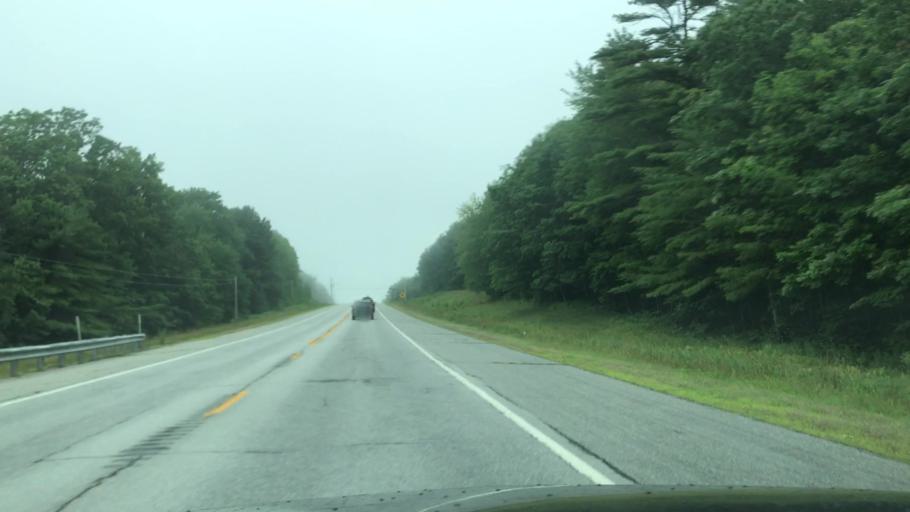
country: US
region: Maine
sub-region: Lincoln County
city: Nobleboro
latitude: 44.0690
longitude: -69.4858
